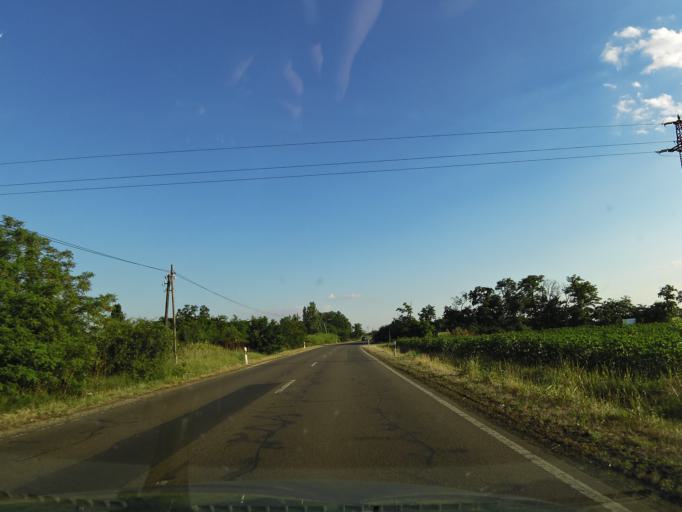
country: HU
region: Jasz-Nagykun-Szolnok
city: Tiszafoldvar
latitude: 47.0124
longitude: 20.2901
